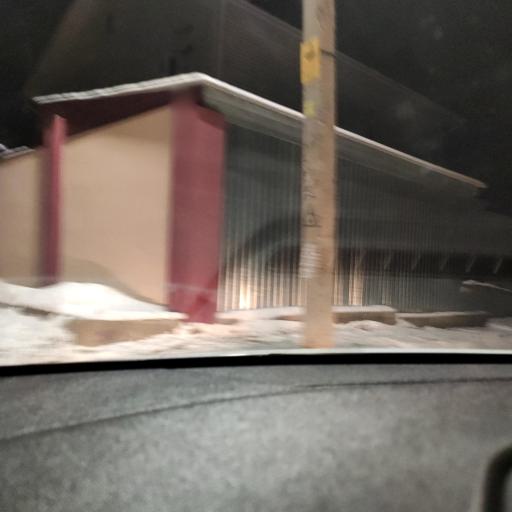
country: RU
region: Tatarstan
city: Stolbishchi
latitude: 55.7562
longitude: 49.2527
